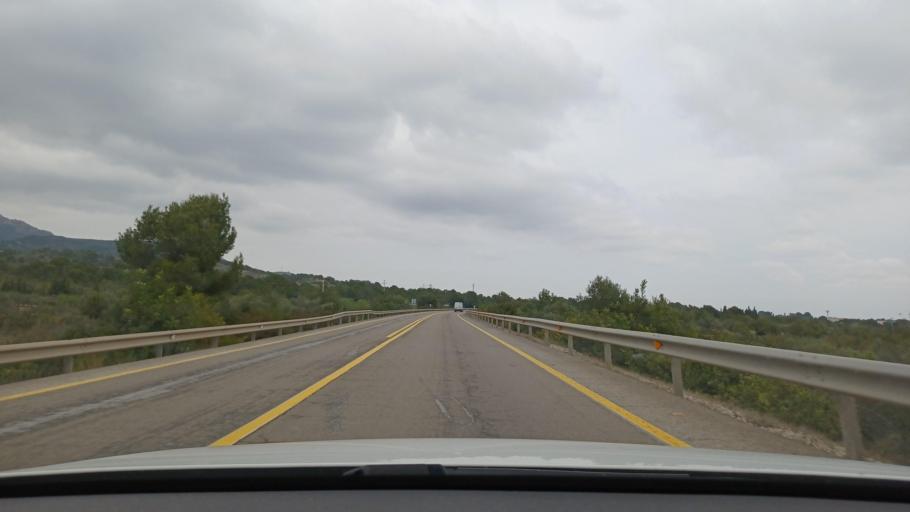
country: ES
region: Catalonia
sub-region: Provincia de Tarragona
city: Sant Carles de la Rapita
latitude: 40.5954
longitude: 0.5565
